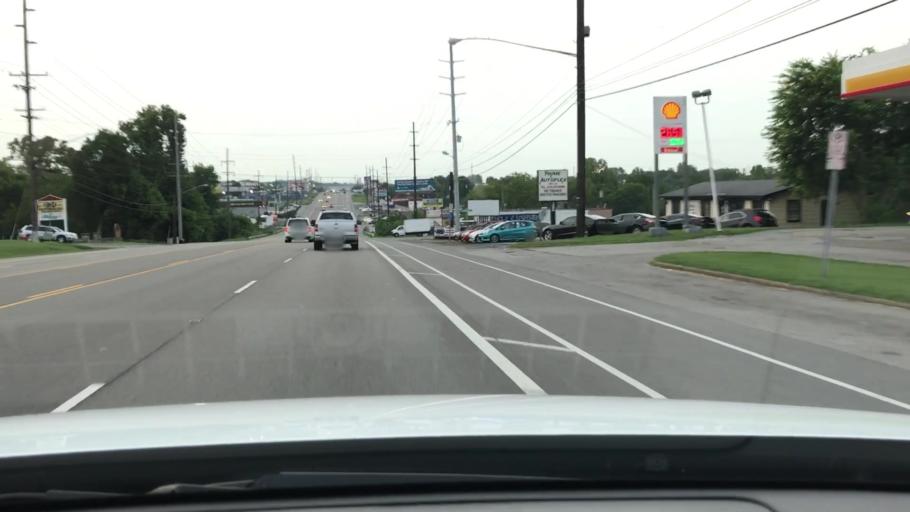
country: US
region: Tennessee
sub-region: Davidson County
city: Goodlettsville
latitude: 36.2827
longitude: -86.7072
